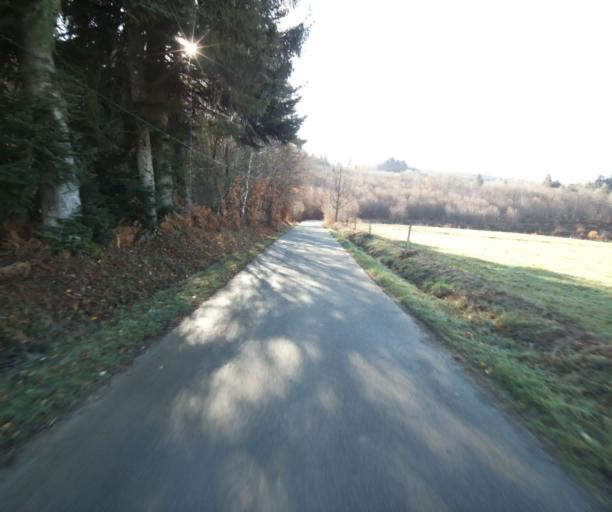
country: FR
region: Limousin
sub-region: Departement de la Correze
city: Sainte-Fortunade
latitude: 45.2114
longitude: 1.7883
